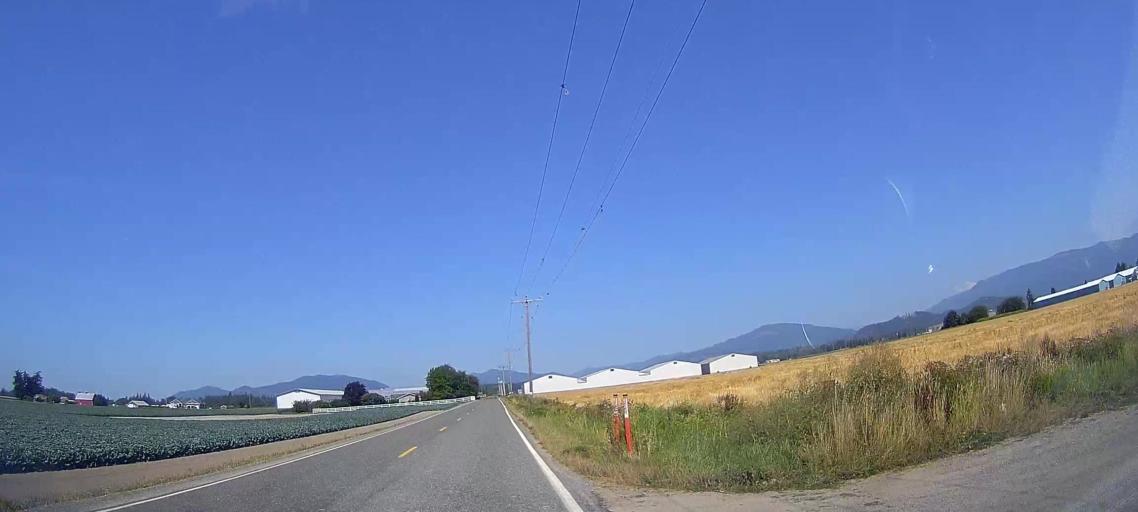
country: US
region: Washington
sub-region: Skagit County
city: Burlington
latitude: 48.4899
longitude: -122.3567
